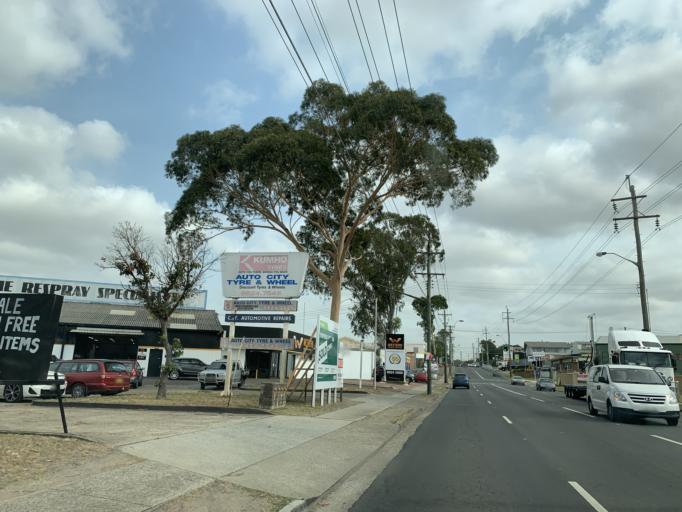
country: AU
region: New South Wales
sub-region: Holroyd
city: Girraween
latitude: -33.7724
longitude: 150.9439
